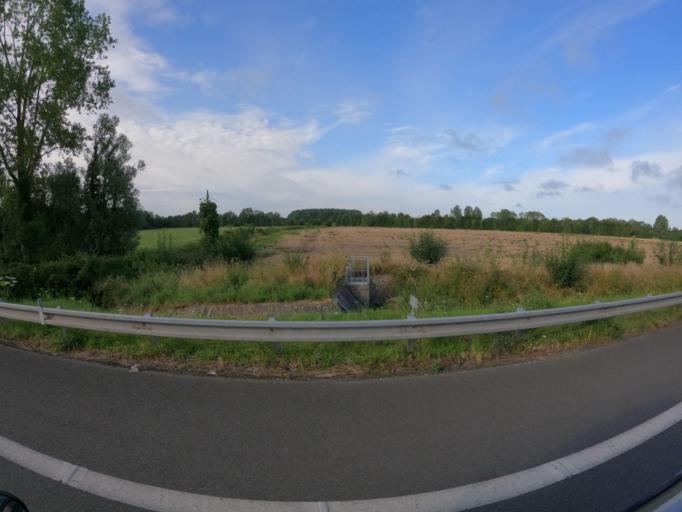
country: FR
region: Pays de la Loire
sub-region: Departement de Maine-et-Loire
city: Allonnes
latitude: 47.2918
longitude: -0.0153
